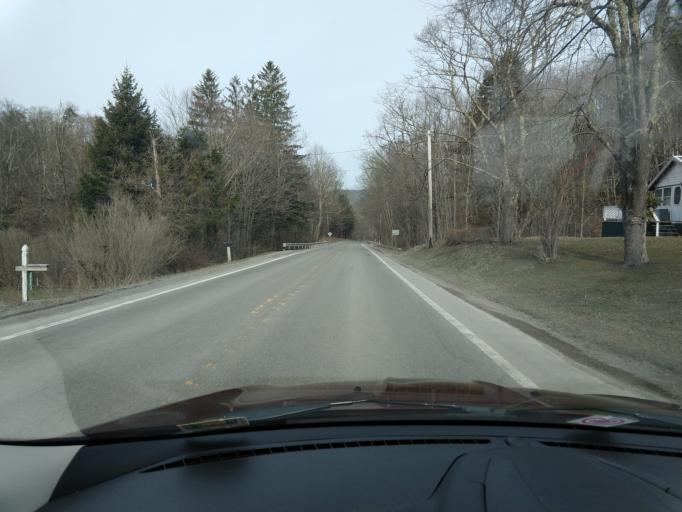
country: US
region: West Virginia
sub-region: Tucker County
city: Parsons
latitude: 38.9020
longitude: -79.4868
